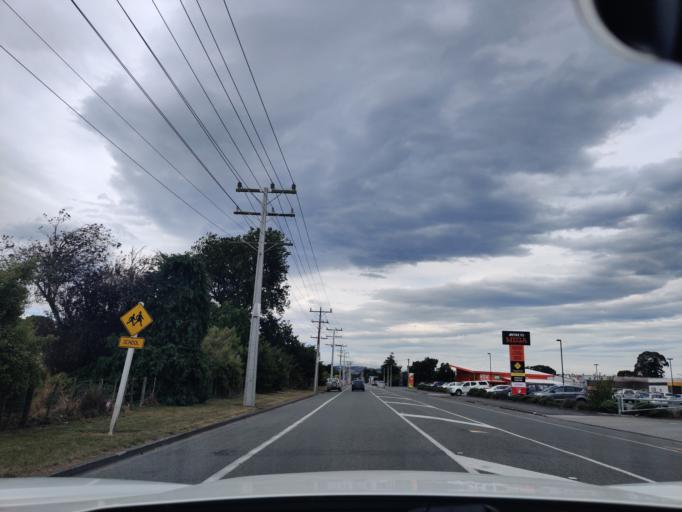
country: NZ
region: Wellington
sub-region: Masterton District
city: Masterton
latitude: -40.9483
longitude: 175.6344
